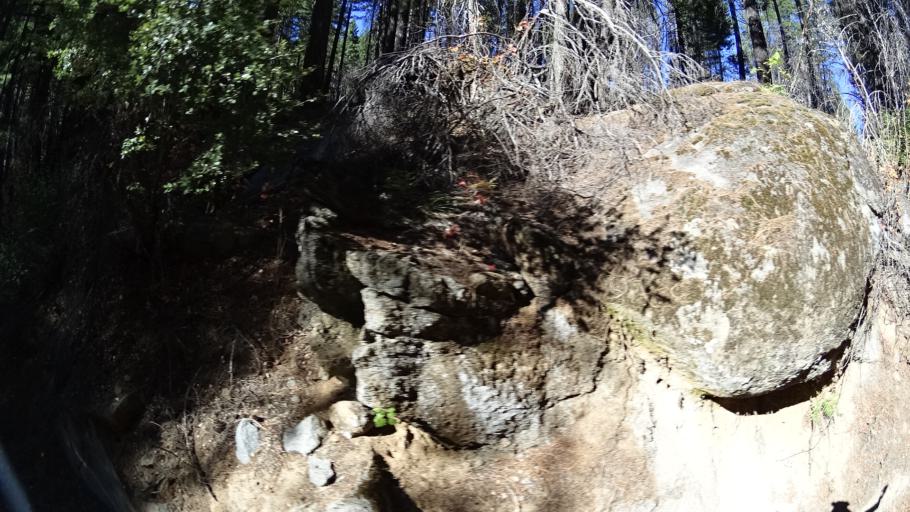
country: US
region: California
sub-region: Siskiyou County
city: Happy Camp
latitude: 41.3092
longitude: -123.2030
